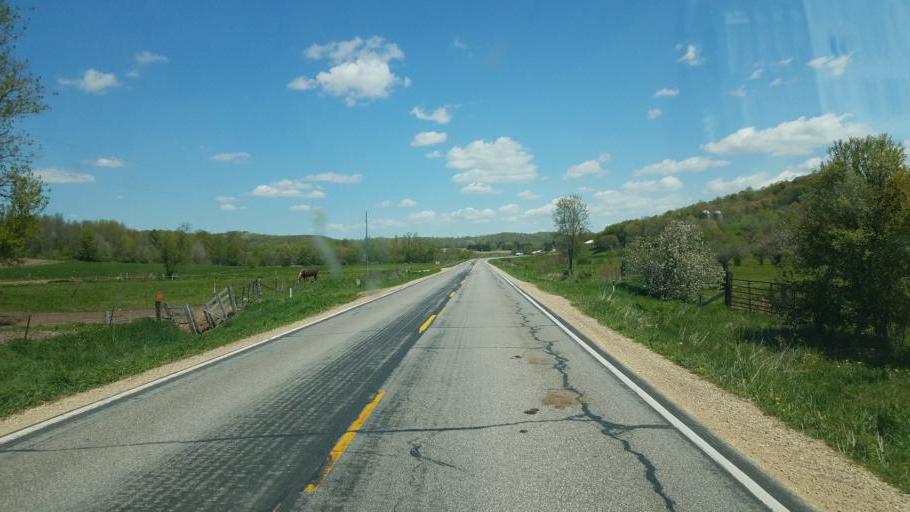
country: US
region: Wisconsin
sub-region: Vernon County
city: Hillsboro
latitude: 43.6501
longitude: -90.3994
